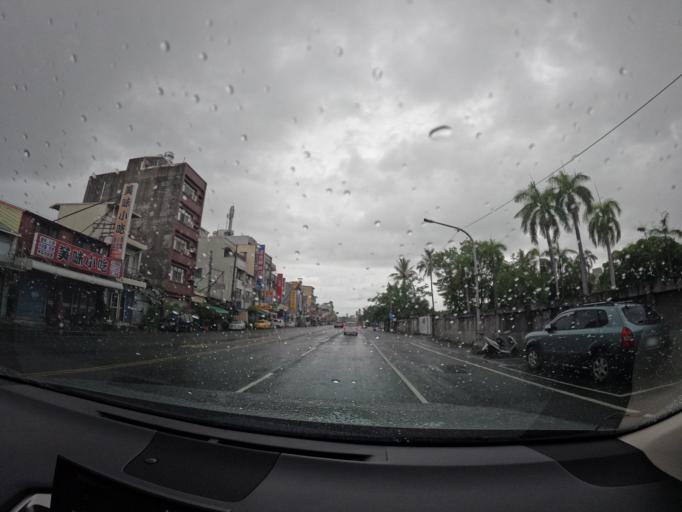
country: TW
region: Taiwan
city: Fengshan
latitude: 22.6435
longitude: 120.3646
